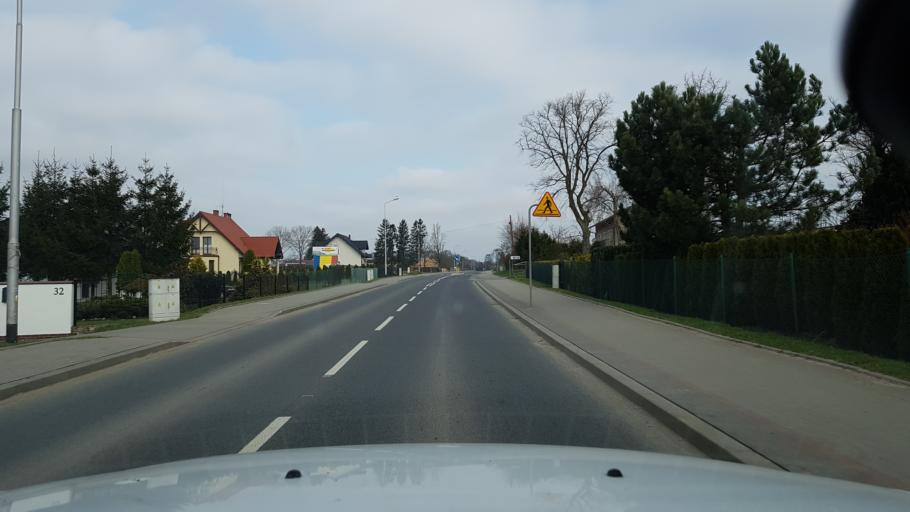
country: PL
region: West Pomeranian Voivodeship
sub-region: Powiat koszalinski
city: Sianow
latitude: 54.2530
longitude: 16.2771
